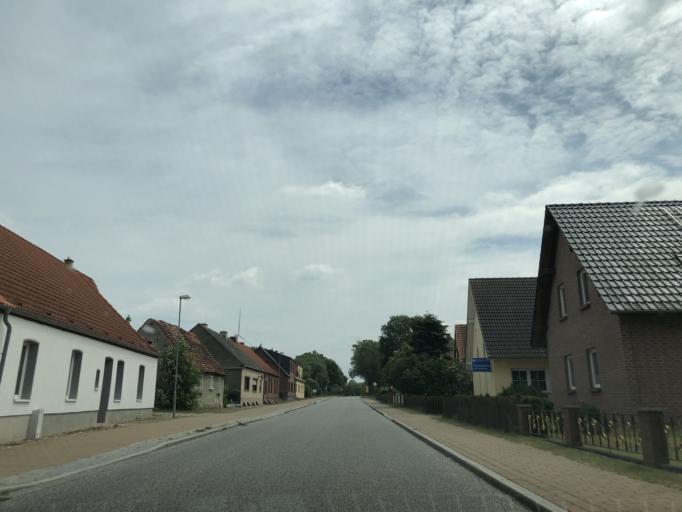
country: DE
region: Brandenburg
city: Gumtow
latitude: 52.9735
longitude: 12.2940
